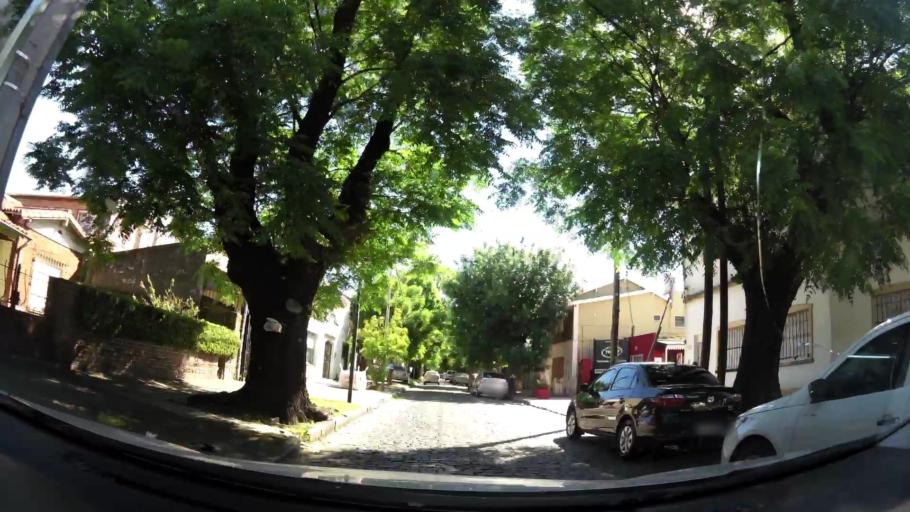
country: AR
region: Buenos Aires
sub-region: Partido de San Isidro
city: San Isidro
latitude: -34.4636
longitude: -58.5304
